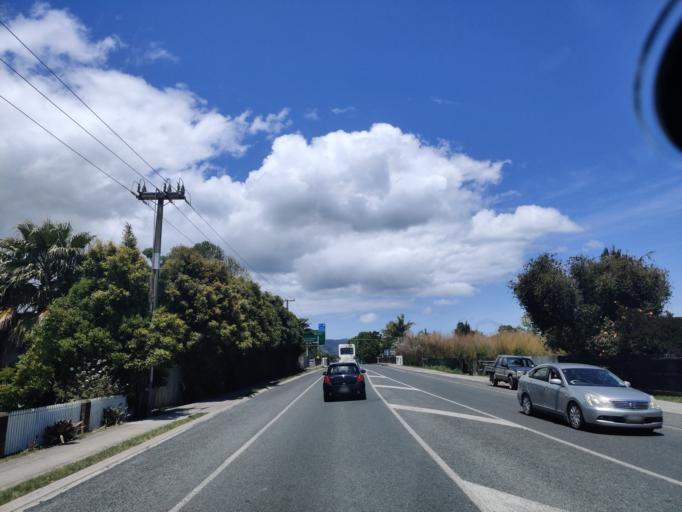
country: NZ
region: Northland
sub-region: Far North District
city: Kaitaia
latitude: -35.1015
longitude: 173.2595
